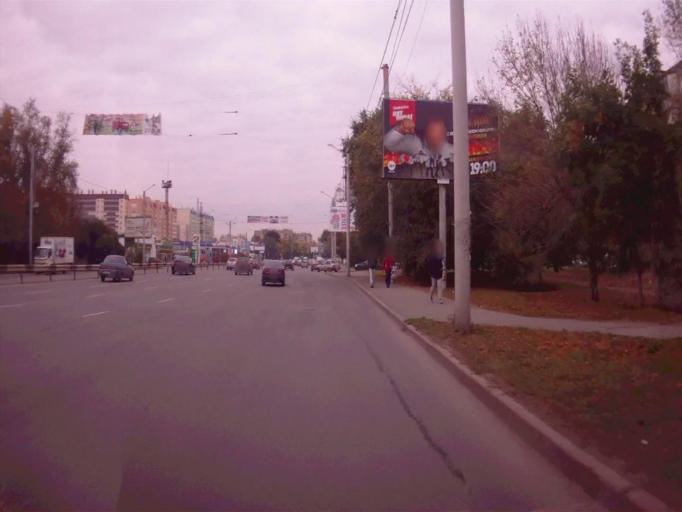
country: RU
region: Chelyabinsk
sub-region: Gorod Chelyabinsk
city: Chelyabinsk
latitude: 55.1377
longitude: 61.4073
